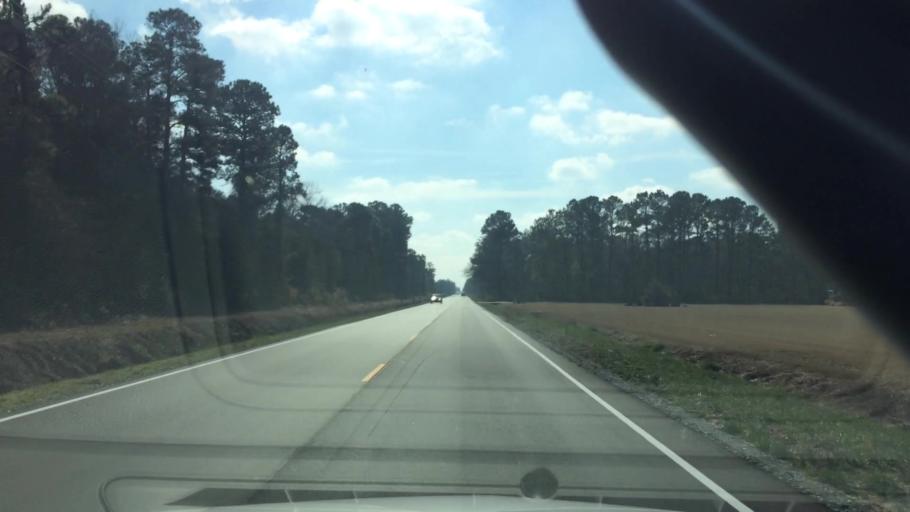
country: US
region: North Carolina
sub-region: Duplin County
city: Beulaville
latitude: 35.0264
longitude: -77.7489
